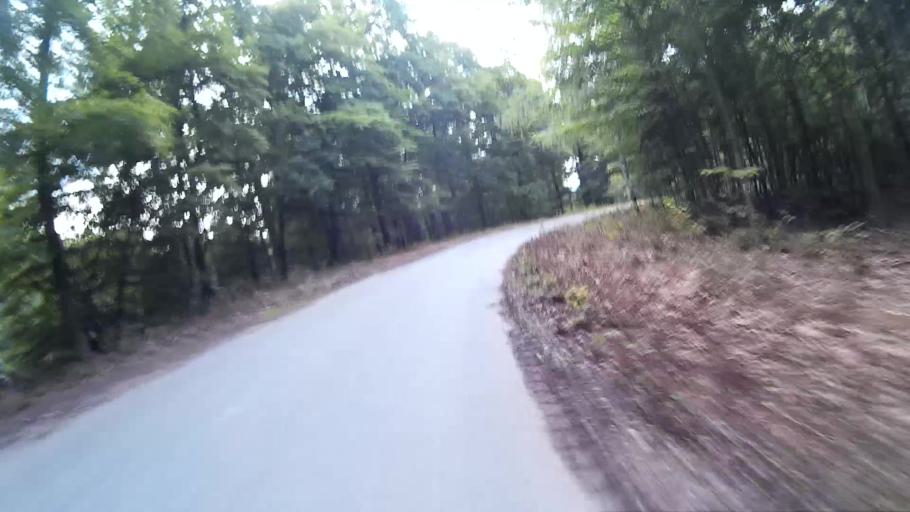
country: CZ
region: South Moravian
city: Veverska Bityska
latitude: 49.2322
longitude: 16.4618
